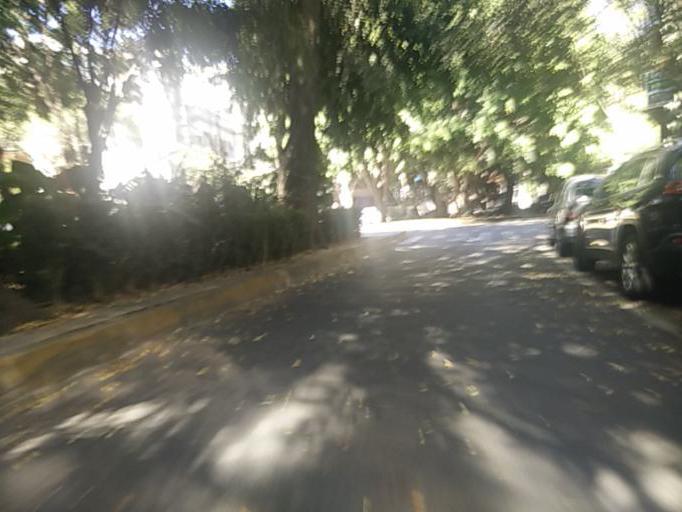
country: MX
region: Mexico City
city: Benito Juarez
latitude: 19.4102
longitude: -99.1717
